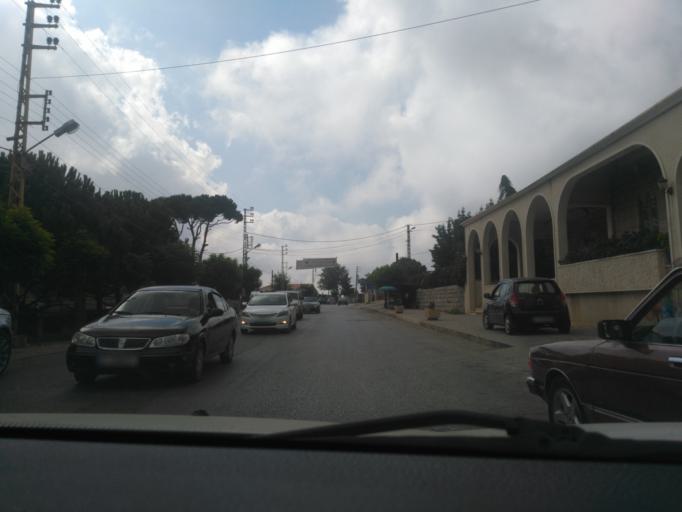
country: LB
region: Mont-Liban
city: Bhamdoun el Mhatta
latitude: 33.8503
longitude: 35.7264
